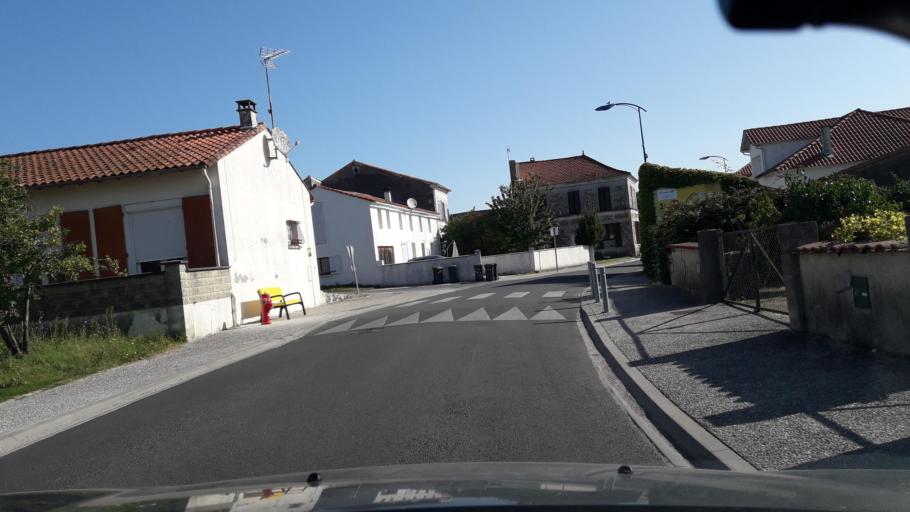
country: FR
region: Poitou-Charentes
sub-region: Departement de la Charente-Maritime
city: Etaules
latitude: 45.7167
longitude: -1.1069
